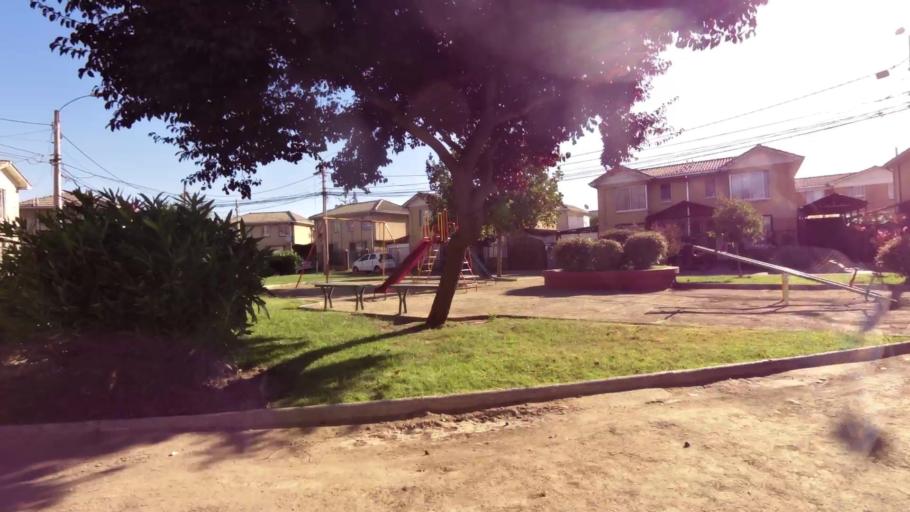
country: CL
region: O'Higgins
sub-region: Provincia de Cachapoal
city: Rancagua
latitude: -34.1777
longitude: -70.7560
